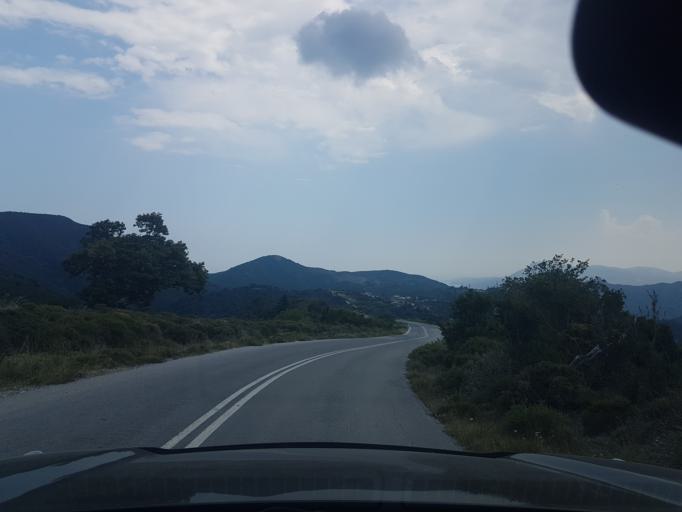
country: GR
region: Central Greece
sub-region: Nomos Evvoias
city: Kymi
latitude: 38.6451
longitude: 24.0577
